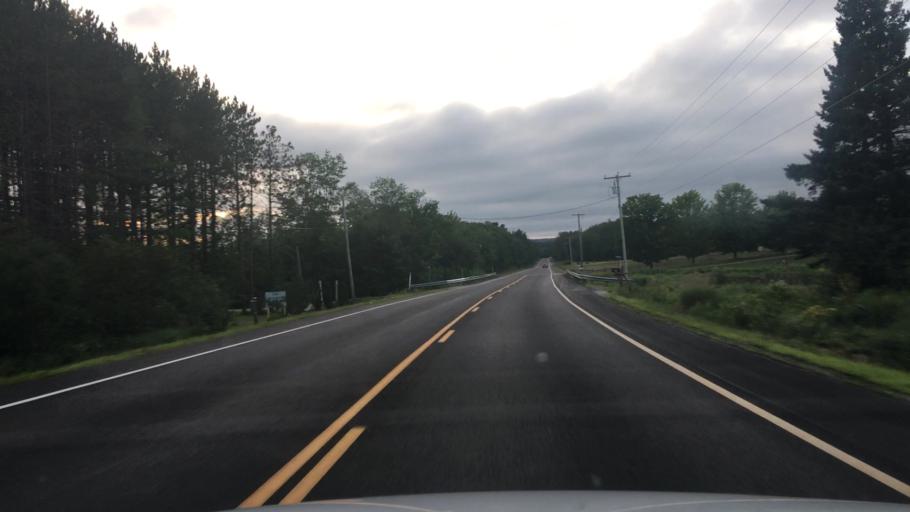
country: US
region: Maine
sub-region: Waldo County
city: Searsmont
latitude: 44.4017
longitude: -69.1634
